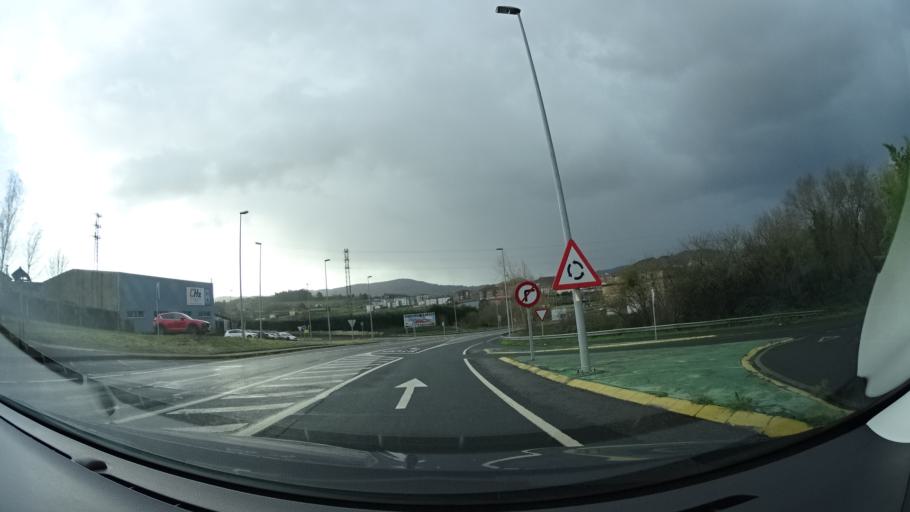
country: ES
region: Basque Country
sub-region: Bizkaia
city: Mungia
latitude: 43.3591
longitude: -2.8353
